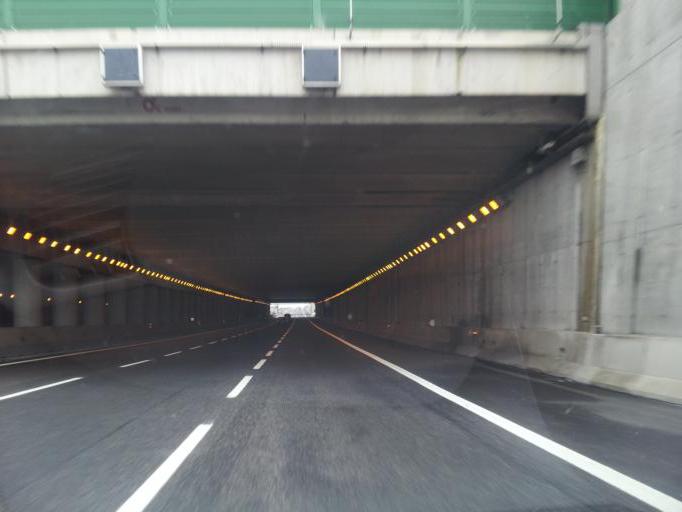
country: IT
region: Veneto
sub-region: Provincia di Venezia
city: Scaltenigo
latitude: 45.4568
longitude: 12.0946
